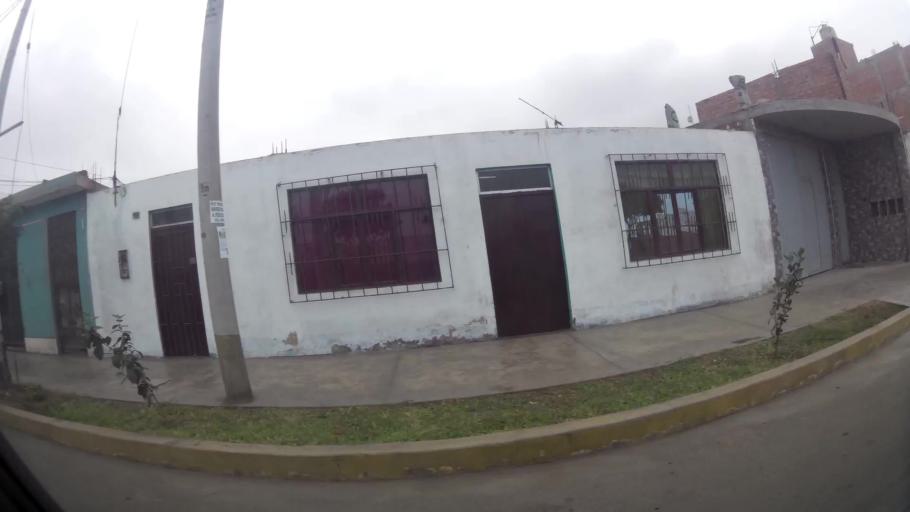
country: PE
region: Lima
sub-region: Provincia de Huaral
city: Chancay
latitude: -11.5635
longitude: -77.2724
